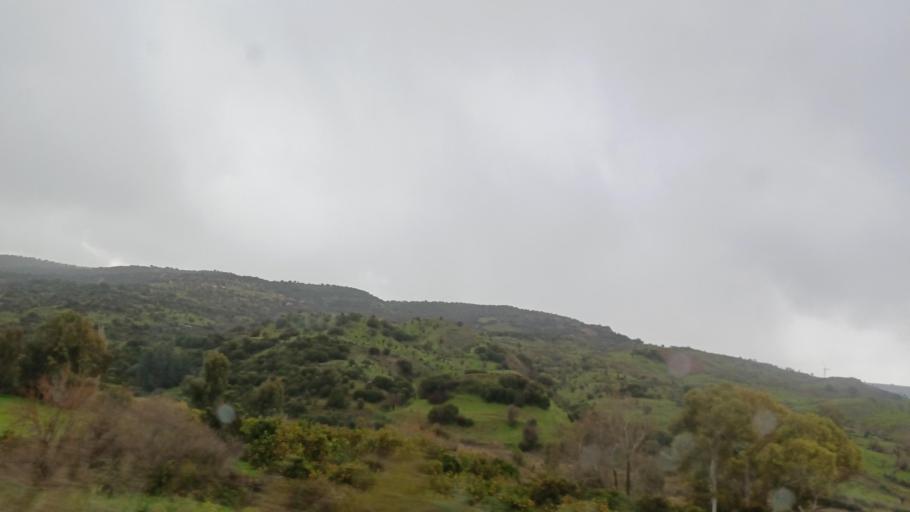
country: CY
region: Limassol
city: Pissouri
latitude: 34.7781
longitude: 32.6570
